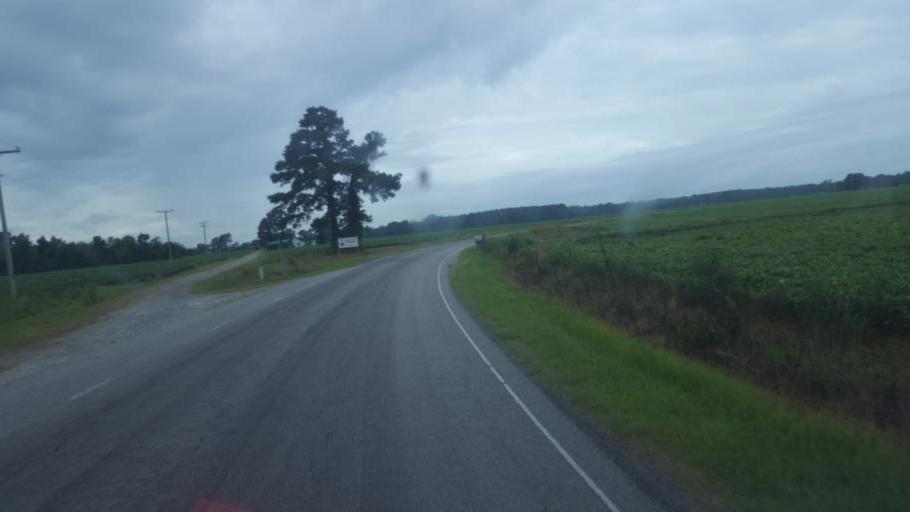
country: US
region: North Carolina
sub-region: Tyrrell County
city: Columbia
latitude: 35.9361
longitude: -76.2758
